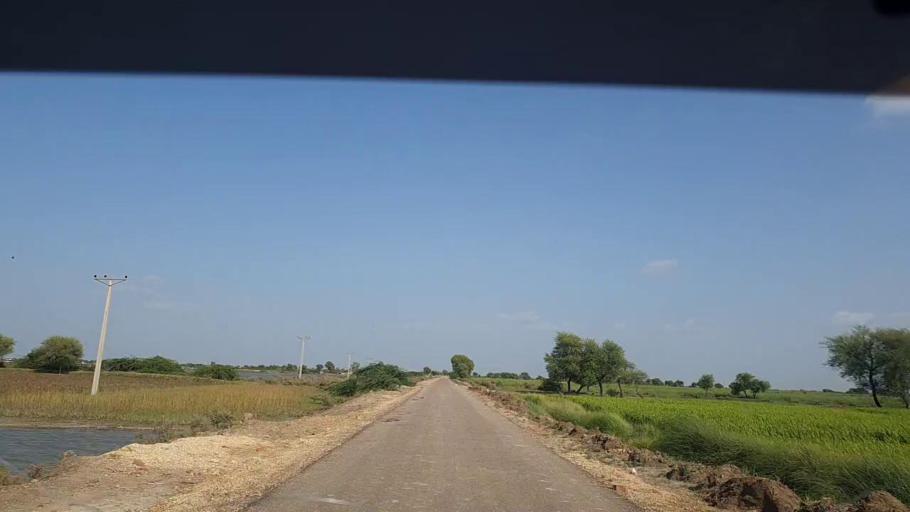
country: PK
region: Sindh
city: Kadhan
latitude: 24.4648
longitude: 68.8406
